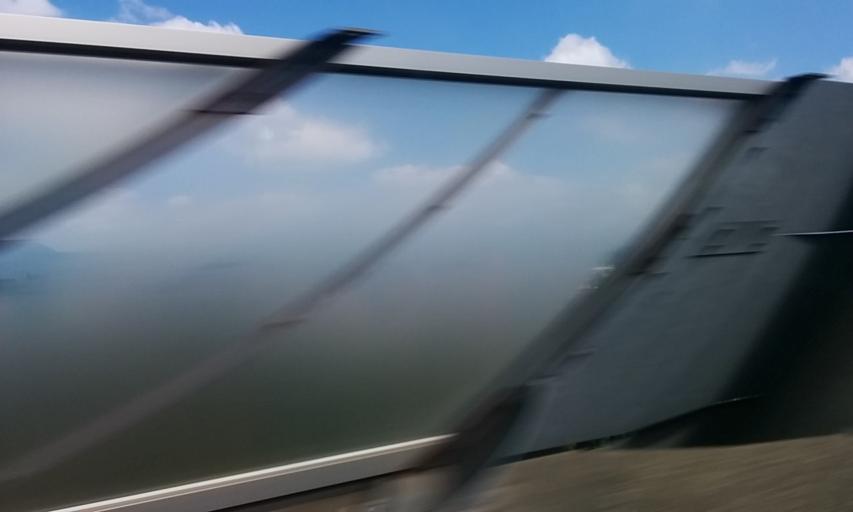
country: JP
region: Tochigi
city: Otawara
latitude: 36.8764
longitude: 139.9809
